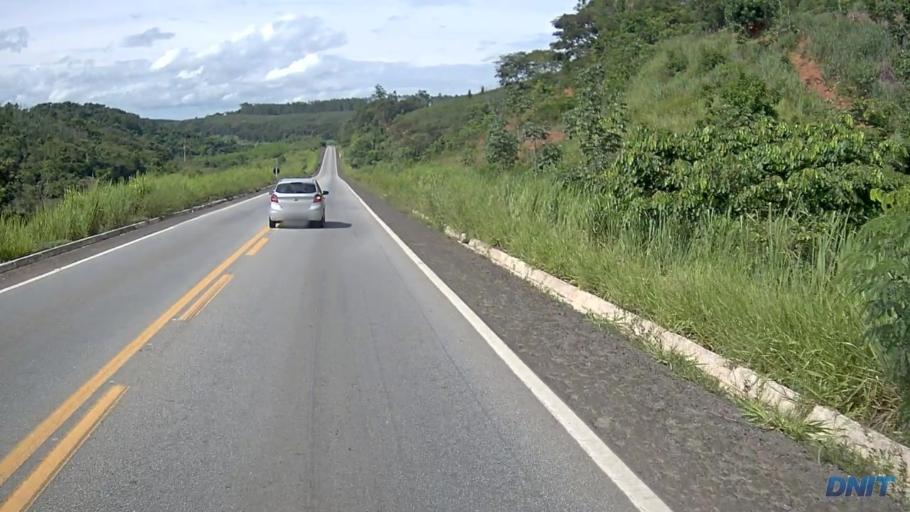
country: BR
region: Minas Gerais
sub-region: Ipaba
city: Ipaba
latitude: -19.4129
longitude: -42.4905
